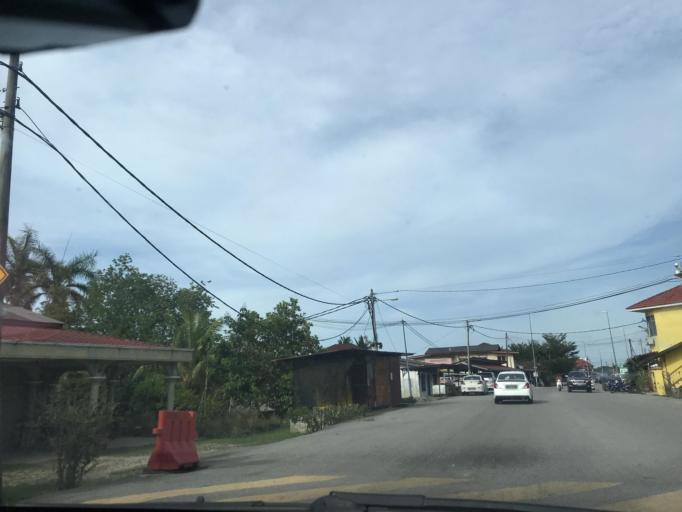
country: MY
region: Kelantan
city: Kota Bharu
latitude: 6.1380
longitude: 102.2116
